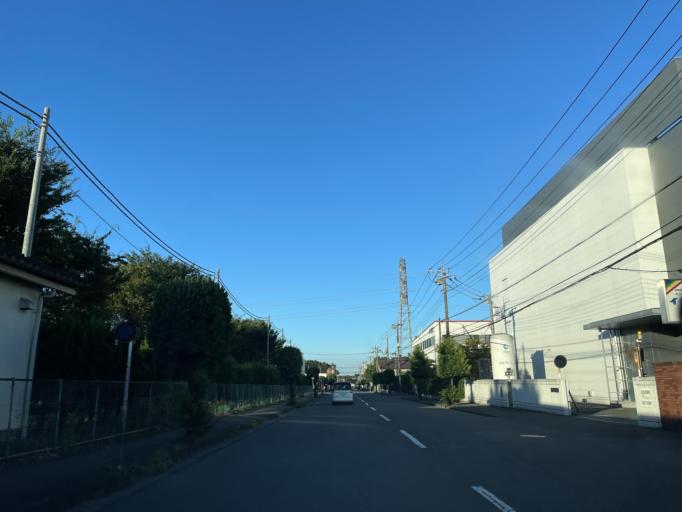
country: JP
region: Saitama
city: Sayama
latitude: 35.8099
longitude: 139.3699
